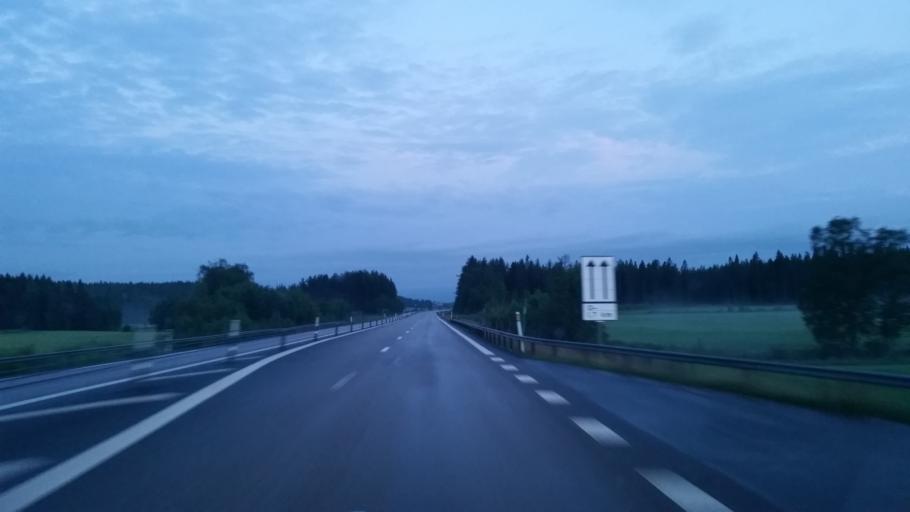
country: SE
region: Vaesterbotten
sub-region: Robertsfors Kommun
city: Robertsfors
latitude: 64.1170
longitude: 20.8811
